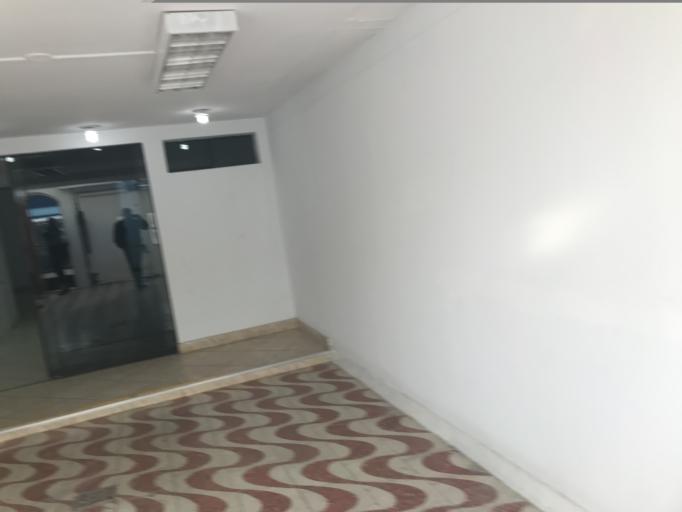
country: PE
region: Lambayeque
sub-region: Provincia de Chiclayo
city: Chiclayo
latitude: -6.7843
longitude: -79.8435
